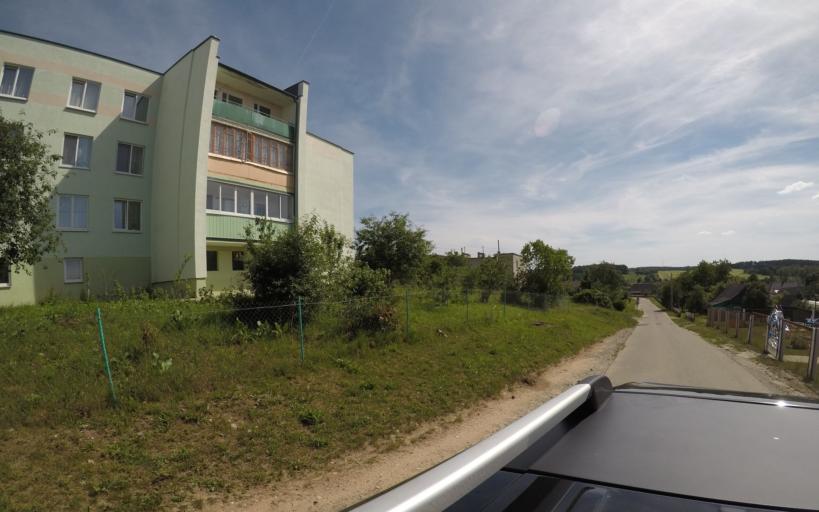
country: BY
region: Grodnenskaya
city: Hal'shany
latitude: 54.2566
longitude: 26.0175
